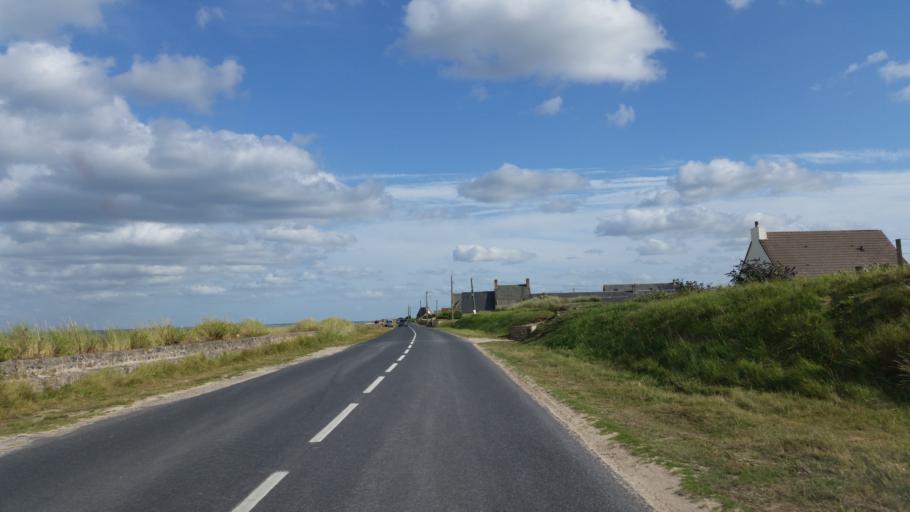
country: FR
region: Lower Normandy
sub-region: Departement de la Manche
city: Sainte-Mere-Eglise
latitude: 49.4572
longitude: -1.2247
